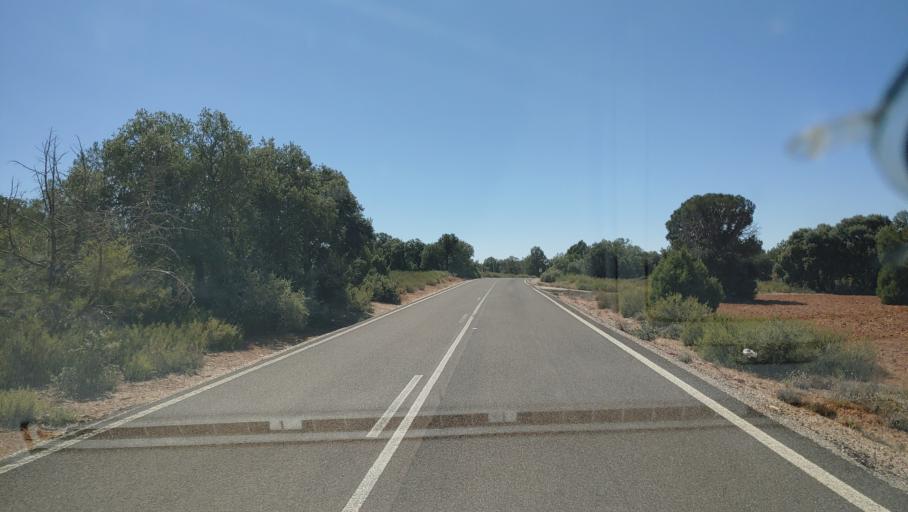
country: ES
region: Castille-La Mancha
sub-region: Provincia de Albacete
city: Ossa de Montiel
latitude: 38.8811
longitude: -2.7780
